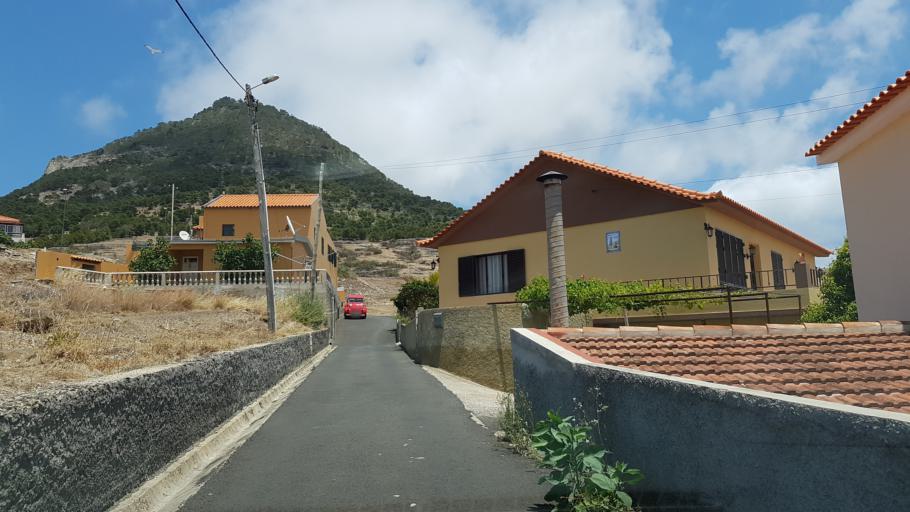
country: PT
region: Madeira
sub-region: Porto Santo
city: Camacha
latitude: 33.0743
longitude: -16.3416
